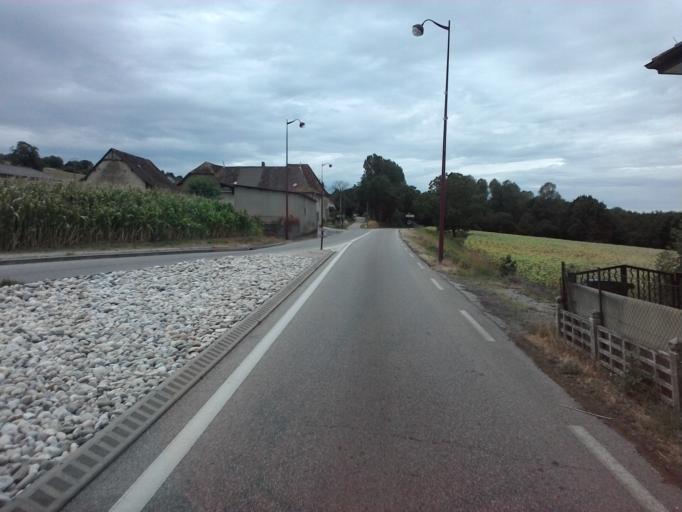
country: FR
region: Rhone-Alpes
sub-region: Departement de l'Isere
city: Thuellin
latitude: 45.6401
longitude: 5.5058
